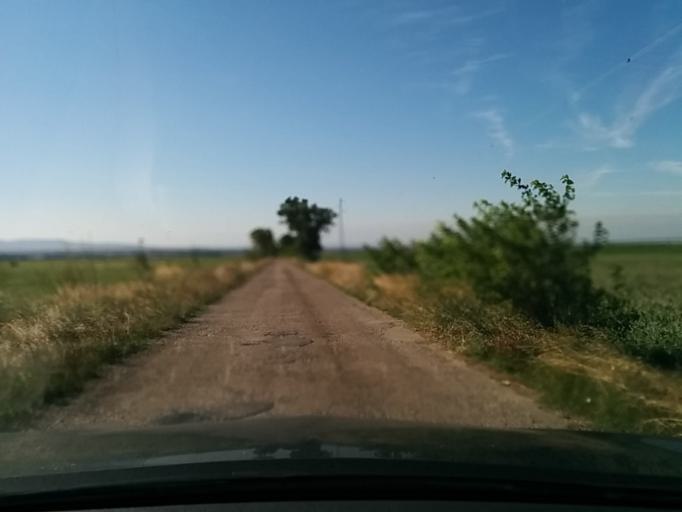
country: ES
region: Aragon
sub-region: Provincia de Zaragoza
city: Tauste
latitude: 42.0023
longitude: -1.2973
